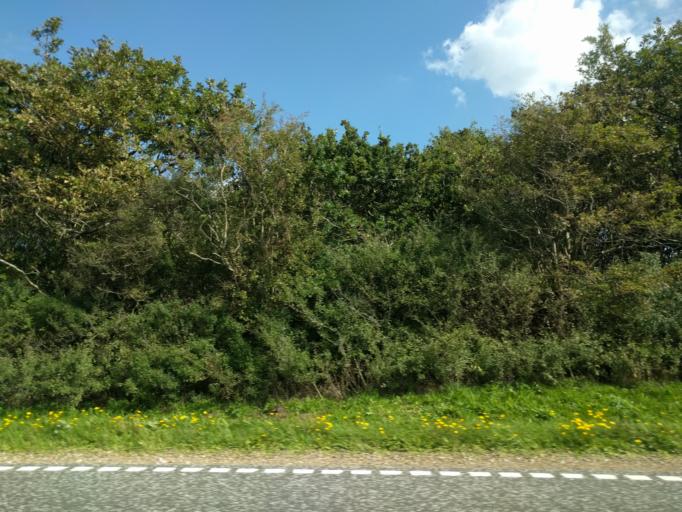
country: DK
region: Central Jutland
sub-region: Skive Kommune
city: Skive
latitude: 56.4597
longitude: 8.9604
